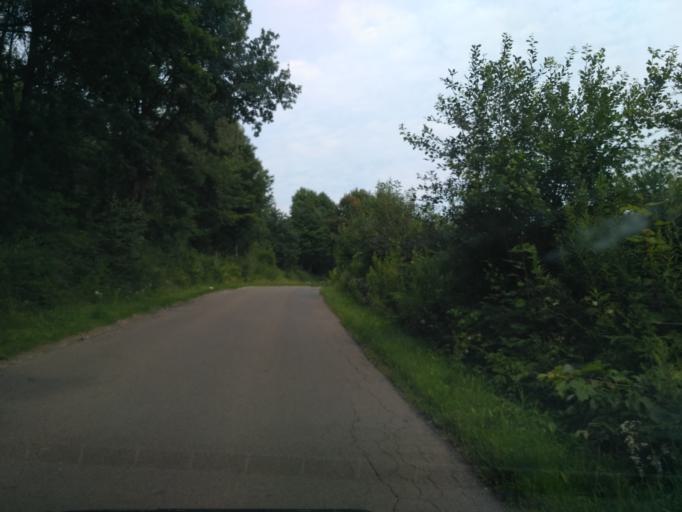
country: PL
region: Subcarpathian Voivodeship
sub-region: Powiat strzyzowski
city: Strzyzow
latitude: 49.8729
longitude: 21.8336
